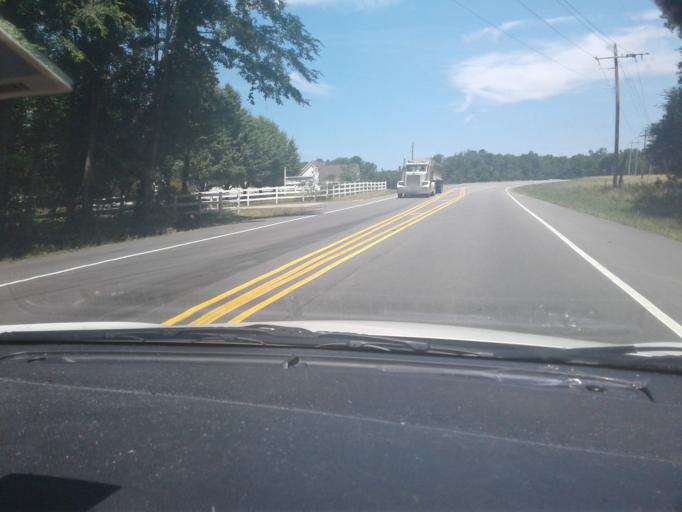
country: US
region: North Carolina
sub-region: Harnett County
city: Lillington
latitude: 35.4344
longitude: -78.8283
